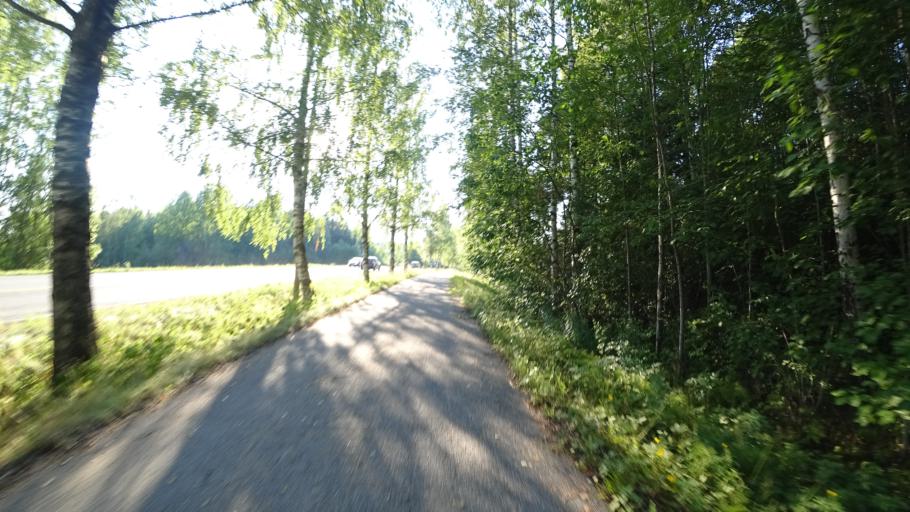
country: FI
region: Pirkanmaa
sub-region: Tampere
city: Nokia
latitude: 61.4712
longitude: 23.3859
